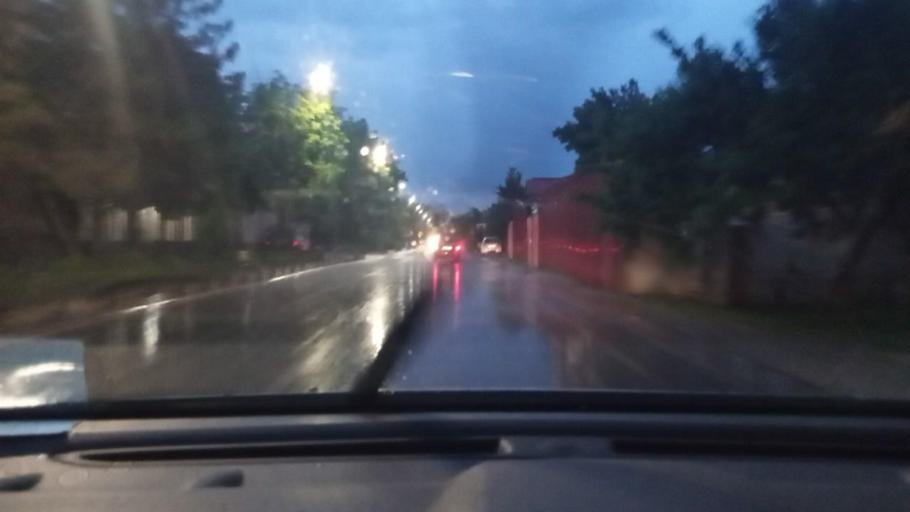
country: UZ
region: Toshkent
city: Salor
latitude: 41.3309
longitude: 69.3565
